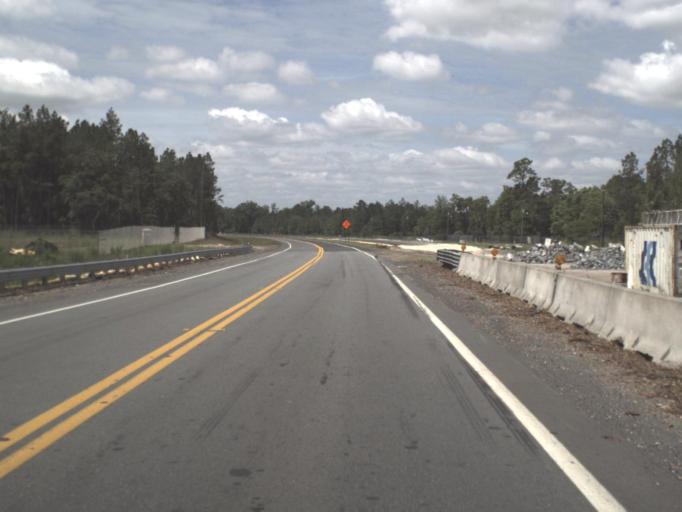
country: US
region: Florida
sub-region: Nassau County
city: Nassau Village-Ratliff
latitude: 30.4760
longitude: -81.9047
